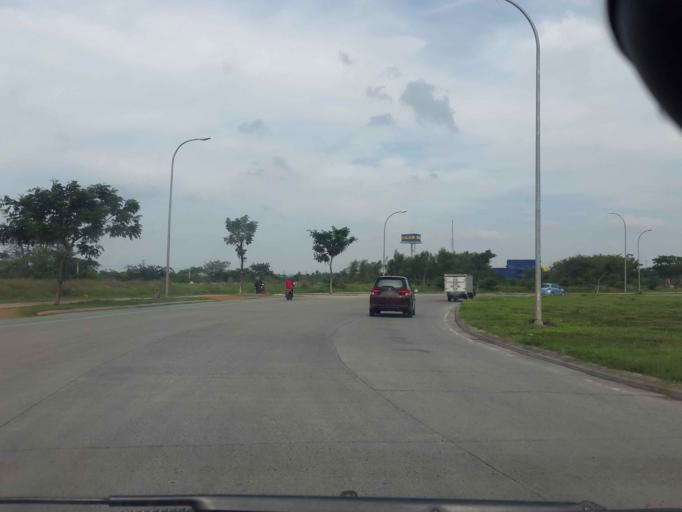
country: ID
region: West Java
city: Ciputat
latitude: -6.2209
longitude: 106.6568
